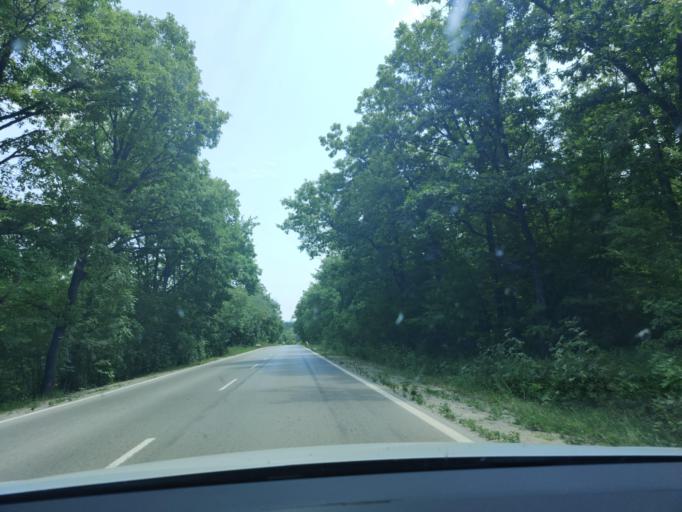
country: BG
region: Montana
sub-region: Obshtina Brusartsi
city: Brusartsi
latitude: 43.4942
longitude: 23.0486
